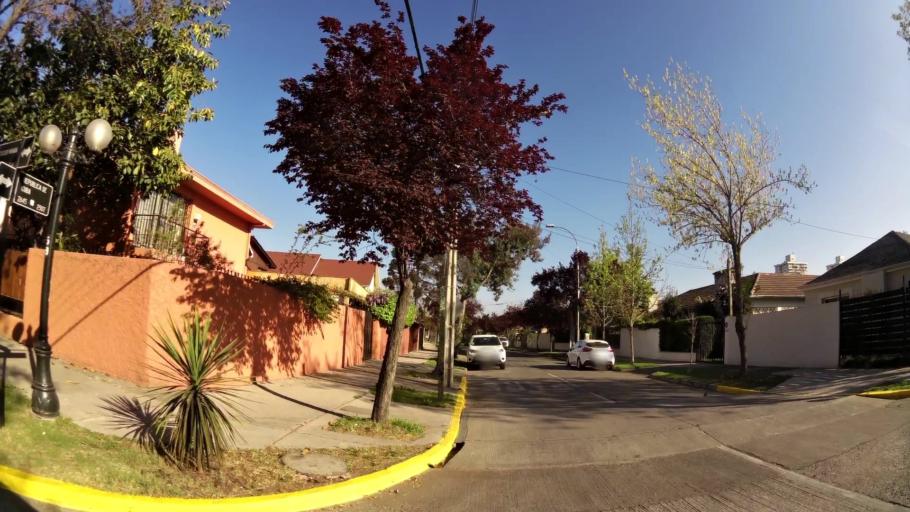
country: CL
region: Santiago Metropolitan
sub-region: Provincia de Santiago
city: Villa Presidente Frei, Nunoa, Santiago, Chile
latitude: -33.4385
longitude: -70.5865
